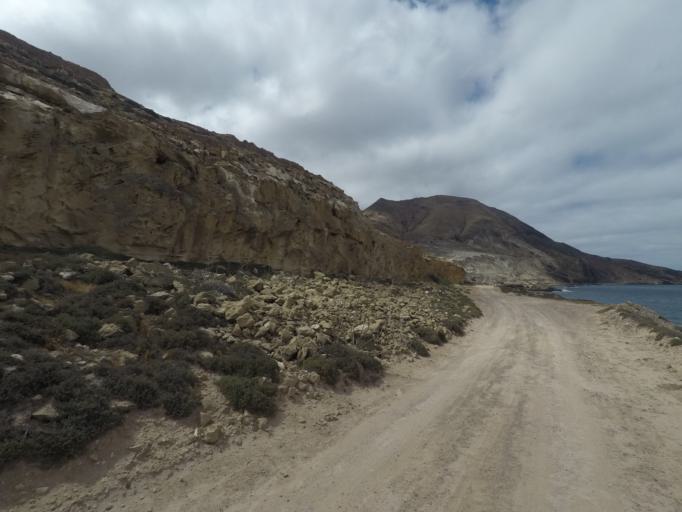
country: PT
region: Madeira
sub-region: Porto Santo
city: Vila de Porto Santo
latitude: 33.0667
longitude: -16.2970
